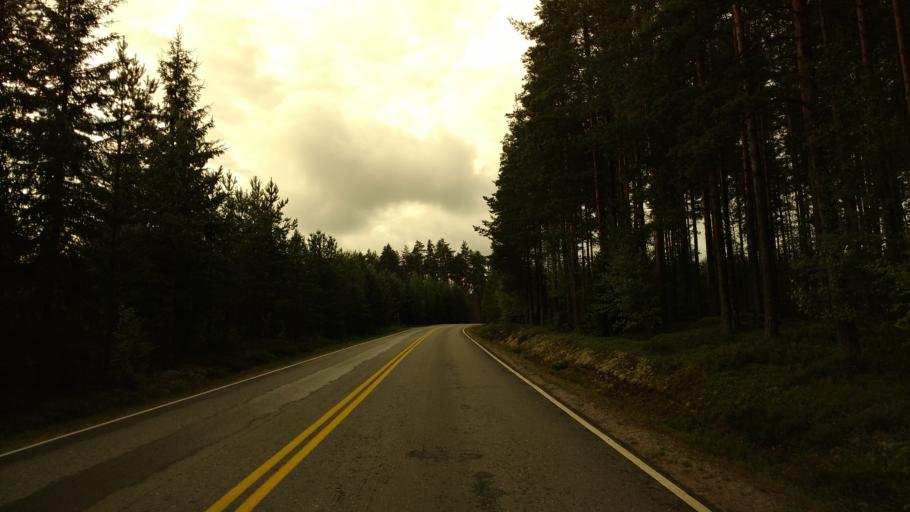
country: FI
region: Varsinais-Suomi
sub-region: Loimaa
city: Koski Tl
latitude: 60.6251
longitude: 23.1119
